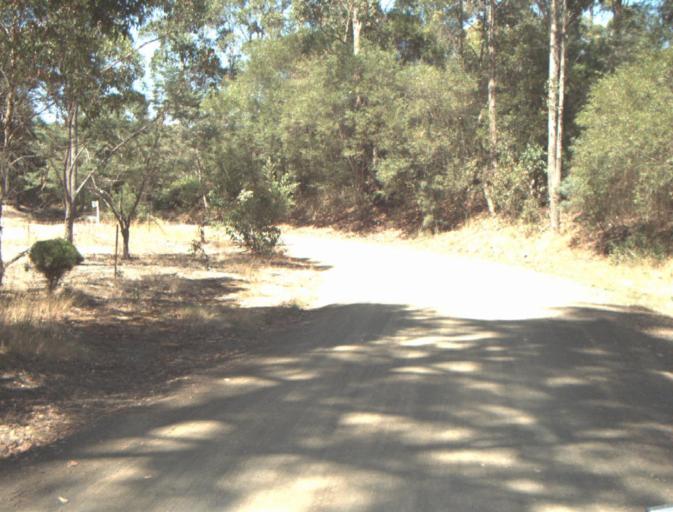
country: AU
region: Tasmania
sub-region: Launceston
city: Mayfield
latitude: -41.2561
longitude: 147.1865
